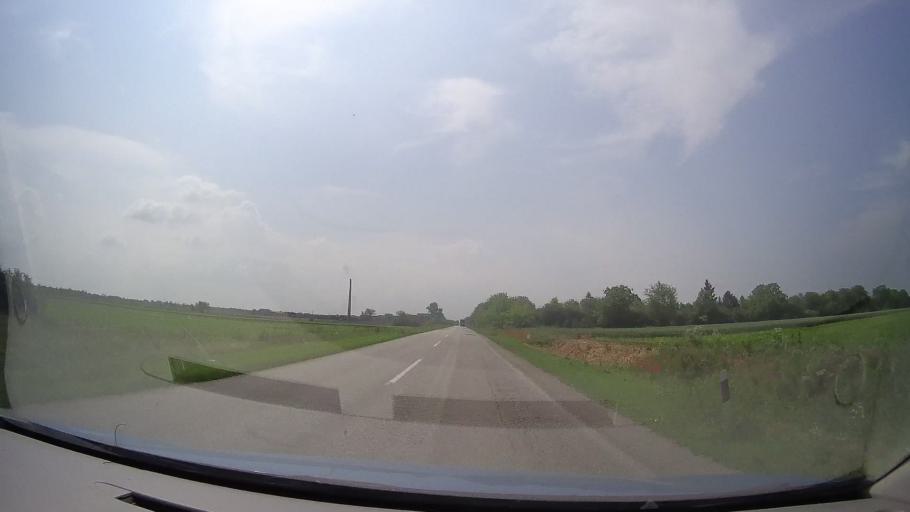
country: RS
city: Crepaja
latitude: 44.9488
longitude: 20.6649
